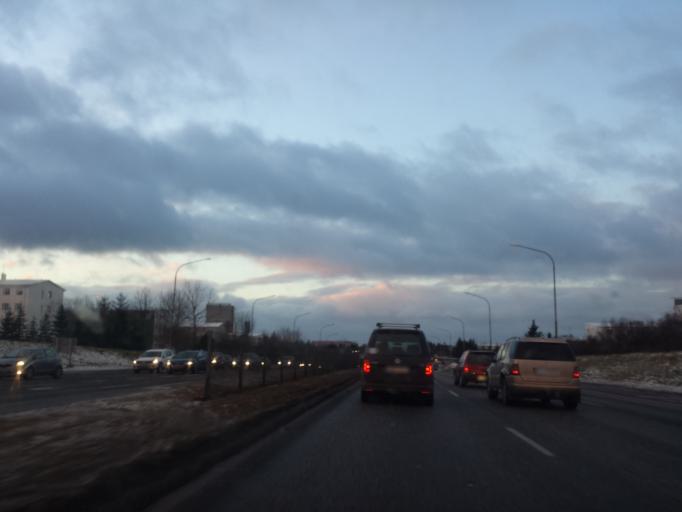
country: IS
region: Capital Region
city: Reykjavik
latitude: 64.1311
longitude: -21.8844
